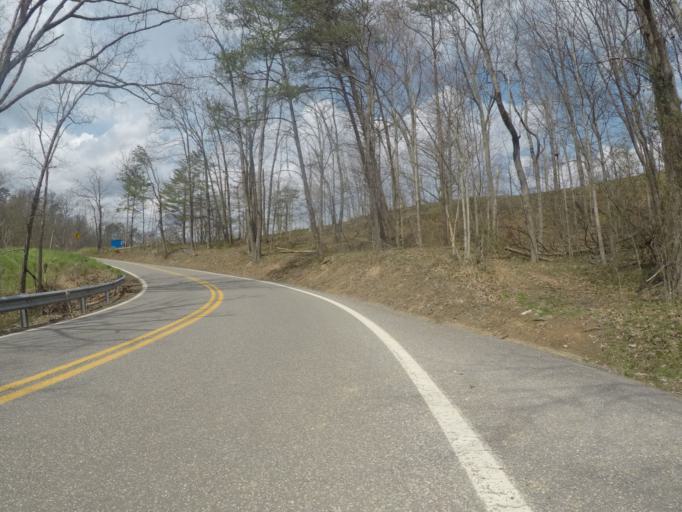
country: US
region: West Virginia
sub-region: Cabell County
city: Pea Ridge
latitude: 38.3517
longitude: -82.3367
